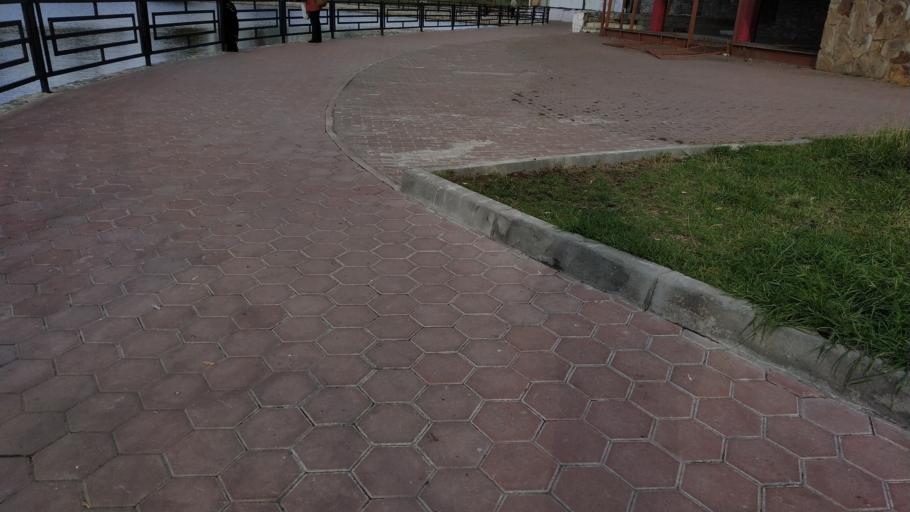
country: RU
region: Moscow
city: Sokol
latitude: 55.8063
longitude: 37.5276
